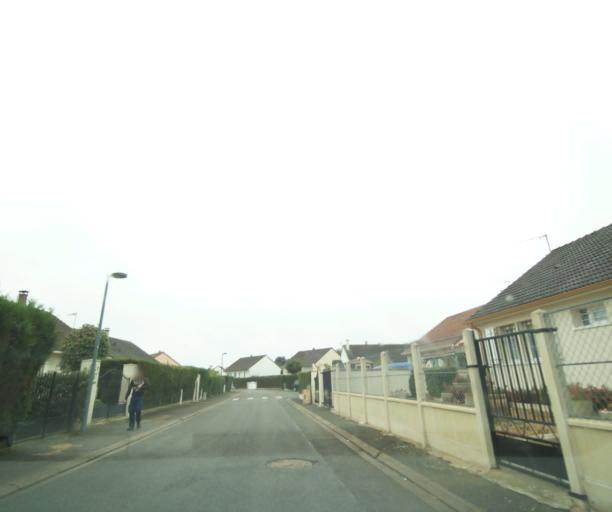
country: FR
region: Centre
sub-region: Departement d'Eure-et-Loir
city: Dreux
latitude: 48.7449
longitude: 1.3506
